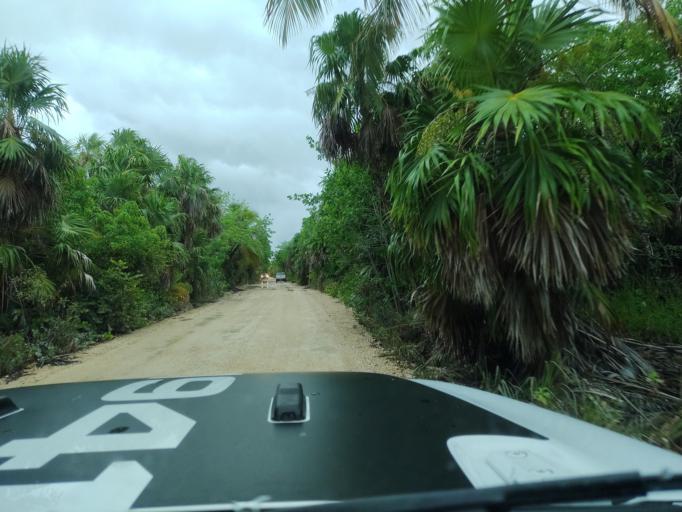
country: MX
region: Quintana Roo
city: Tulum
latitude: 20.0617
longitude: -87.4807
